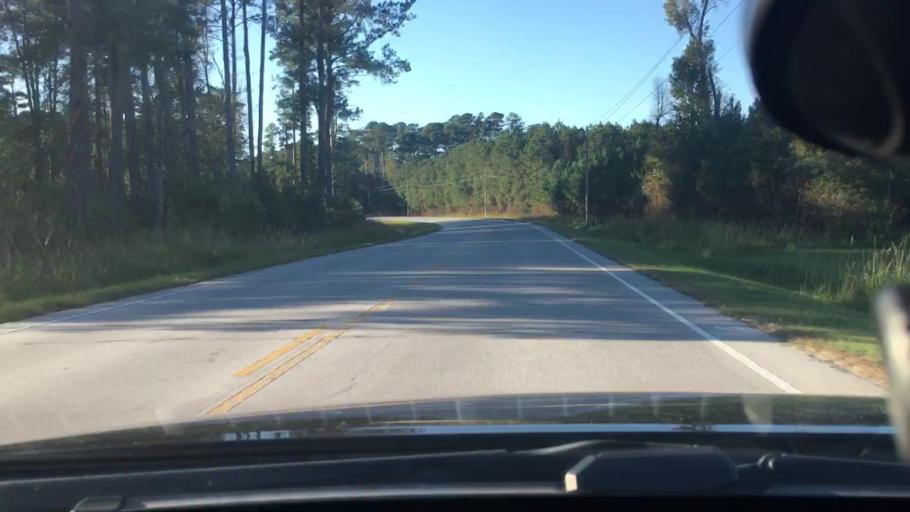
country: US
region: North Carolina
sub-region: Pitt County
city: Windsor
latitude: 35.4681
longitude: -77.2785
